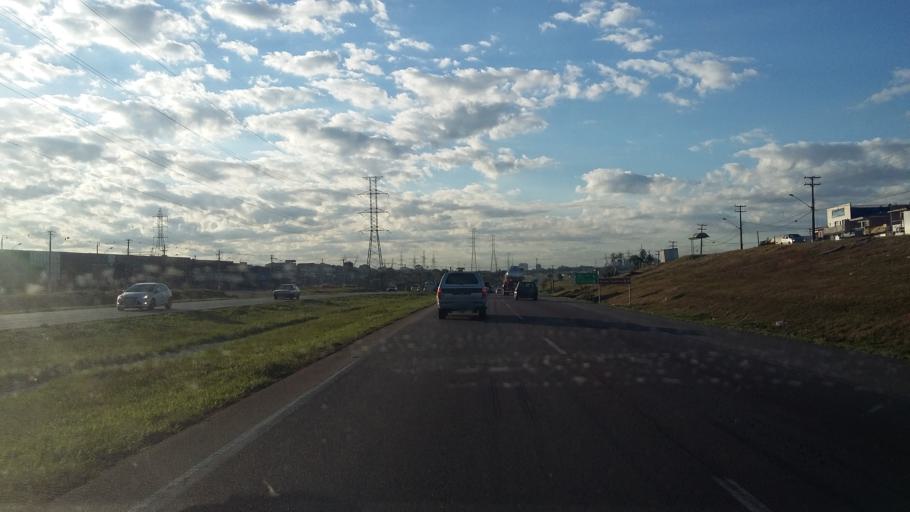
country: BR
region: Parana
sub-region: Curitiba
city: Curitiba
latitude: -25.5071
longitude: -49.3404
